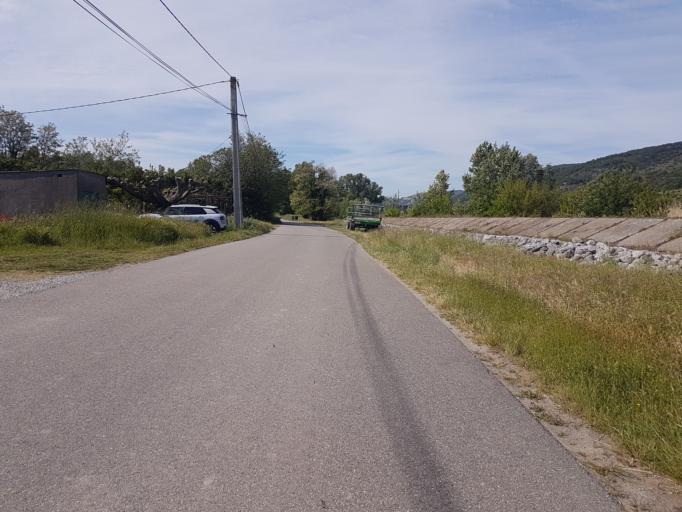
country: FR
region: Rhone-Alpes
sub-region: Departement de l'Ardeche
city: La Voulte-sur-Rhone
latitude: 44.7968
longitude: 4.7839
